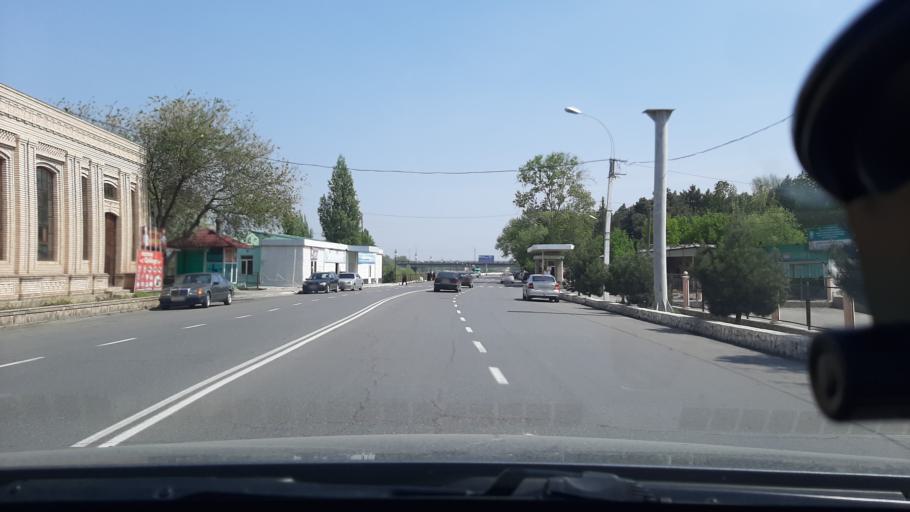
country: TJ
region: Viloyati Sughd
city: Khujand
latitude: 40.2929
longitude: 69.6359
